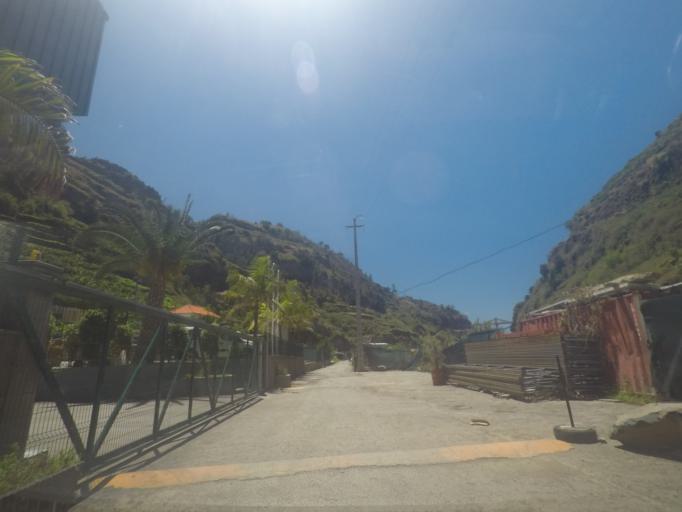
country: PT
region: Madeira
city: Camara de Lobos
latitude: 32.6637
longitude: -16.9604
